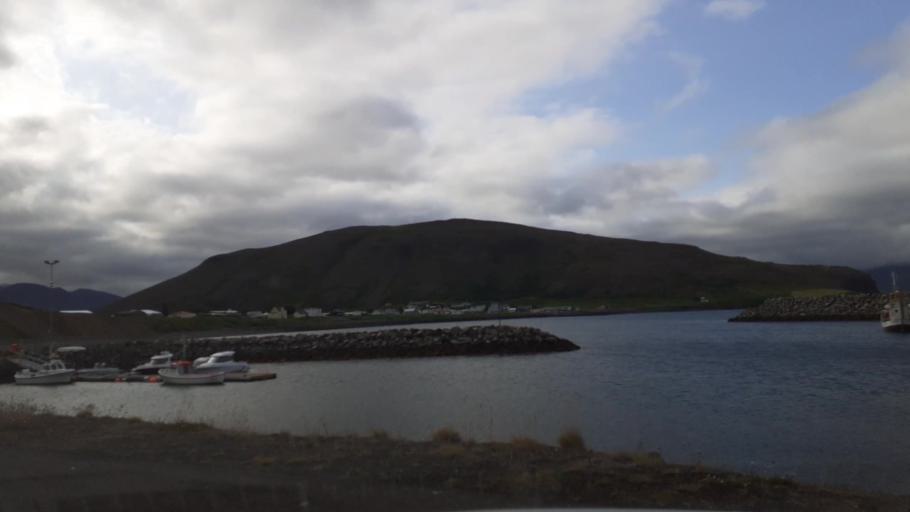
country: IS
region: Northeast
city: Akureyri
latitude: 65.9542
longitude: -18.1853
